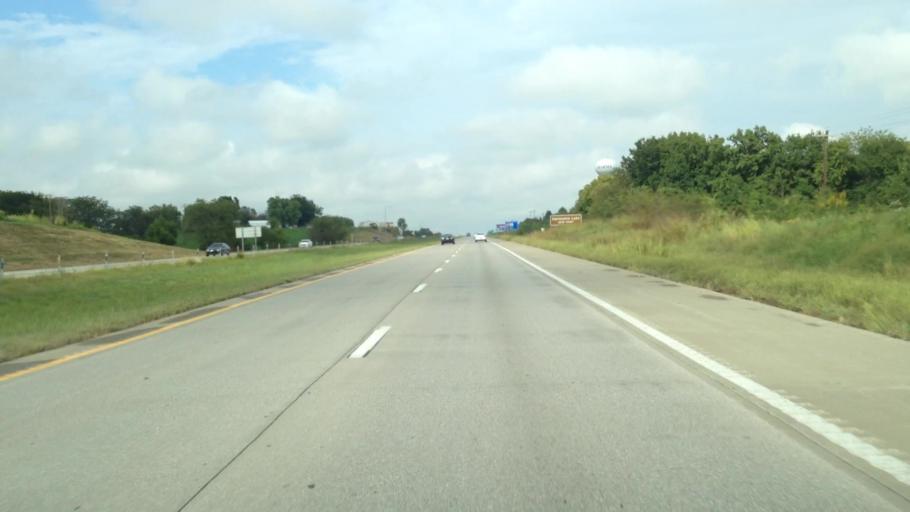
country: US
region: Missouri
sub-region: Clay County
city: Kearney
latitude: 39.3554
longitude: -94.3789
